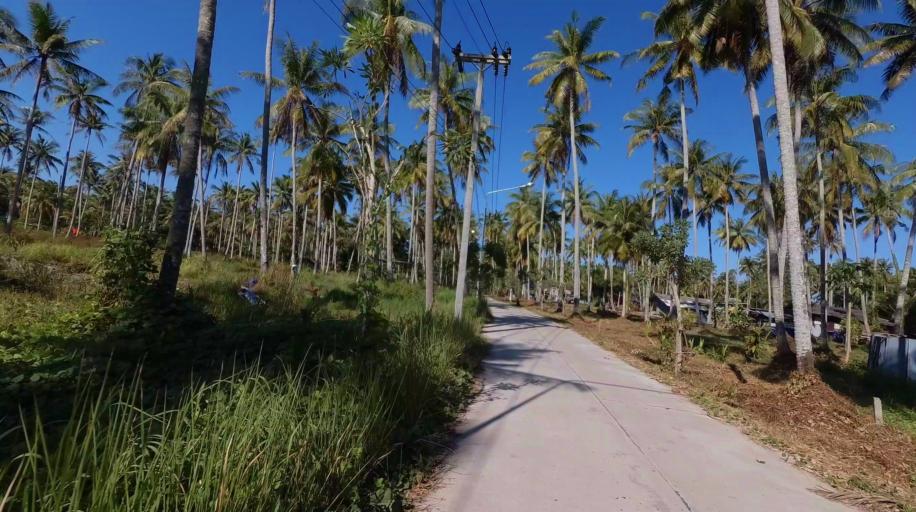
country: TH
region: Trat
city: Ko Kut
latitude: 11.6214
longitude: 102.5492
